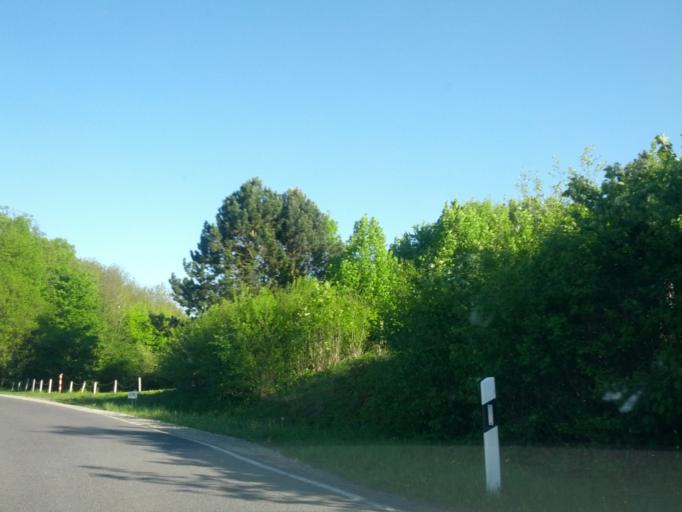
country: DE
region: Thuringia
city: Geismar
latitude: 51.2125
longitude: 10.1647
